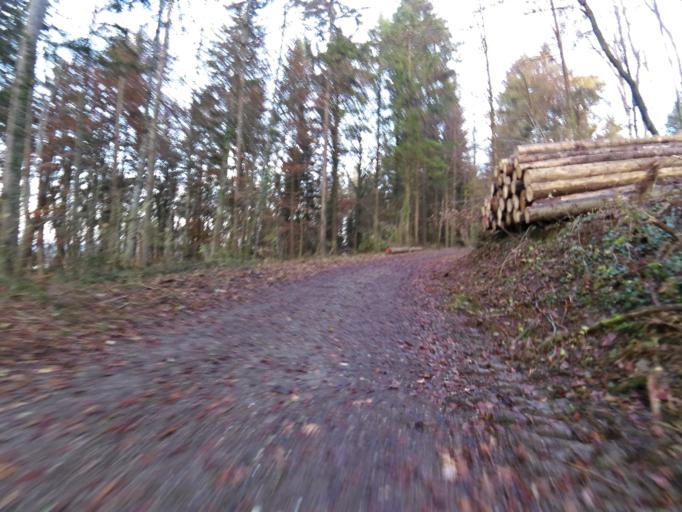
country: CH
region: Thurgau
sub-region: Frauenfeld District
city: Frauenfeld
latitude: 47.5673
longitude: 8.9315
